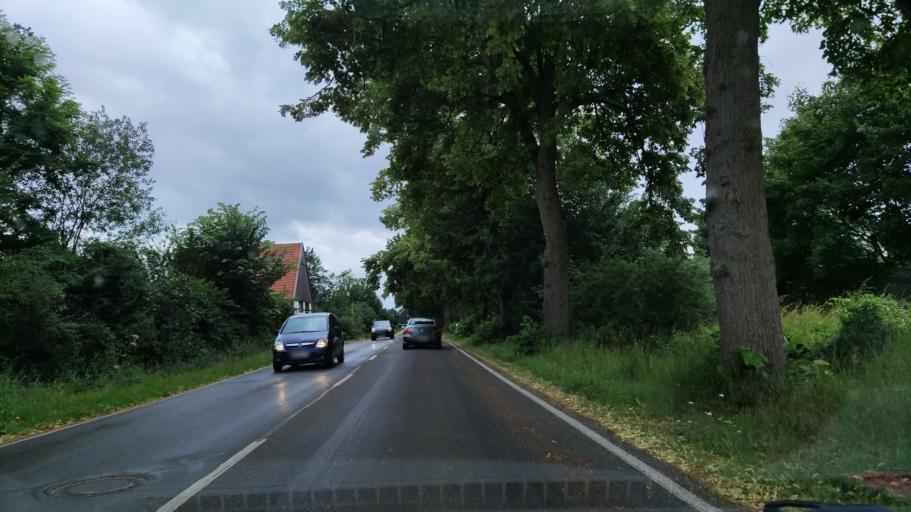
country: DE
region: North Rhine-Westphalia
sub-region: Regierungsbezirk Arnsberg
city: Hamm
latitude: 51.7157
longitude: 7.8404
